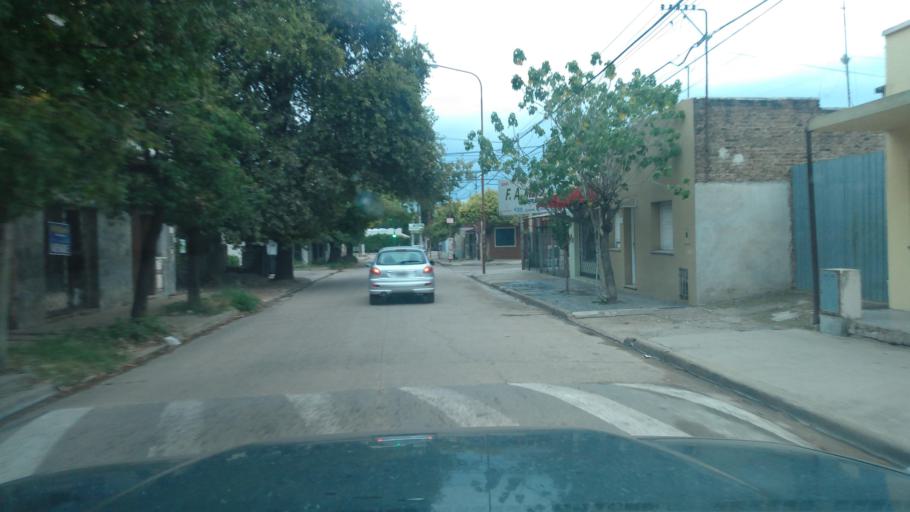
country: AR
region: Buenos Aires
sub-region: Partido de Lujan
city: Lujan
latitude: -34.5653
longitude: -59.0960
